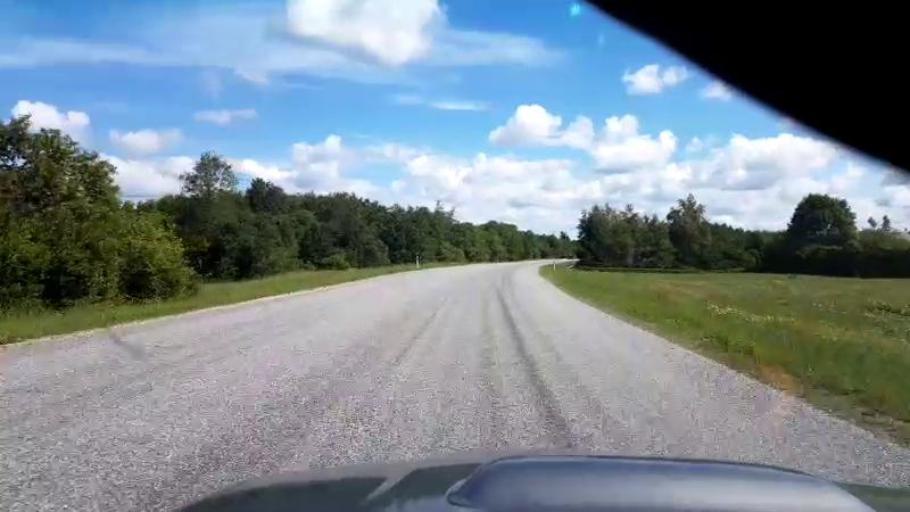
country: EE
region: Laeaene-Virumaa
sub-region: Tapa vald
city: Tapa
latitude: 59.2074
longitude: 25.8524
